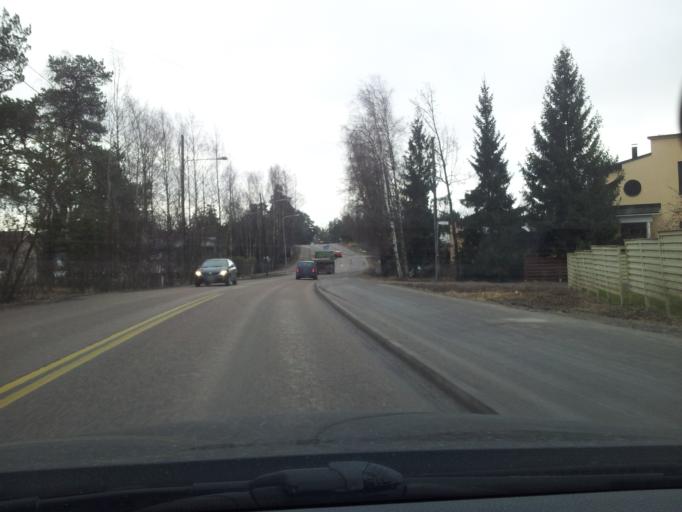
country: FI
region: Uusimaa
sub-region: Helsinki
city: Espoo
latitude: 60.1773
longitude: 24.6854
